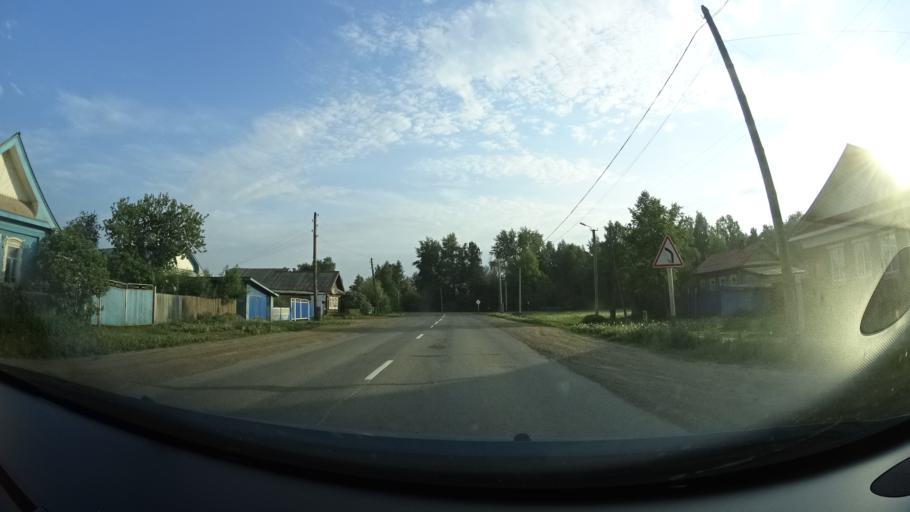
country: RU
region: Perm
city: Barda
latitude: 56.9339
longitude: 55.5927
